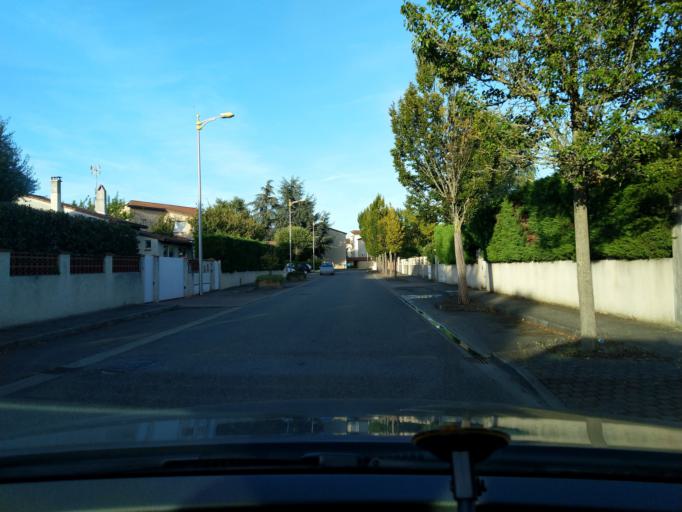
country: FR
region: Midi-Pyrenees
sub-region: Departement de la Haute-Garonne
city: Tournefeuille
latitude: 43.5795
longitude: 1.3371
